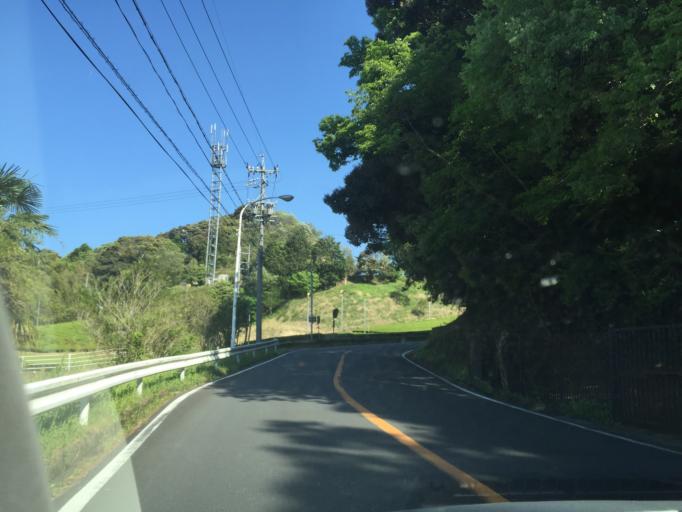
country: JP
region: Shizuoka
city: Kakegawa
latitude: 34.7707
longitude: 138.0518
